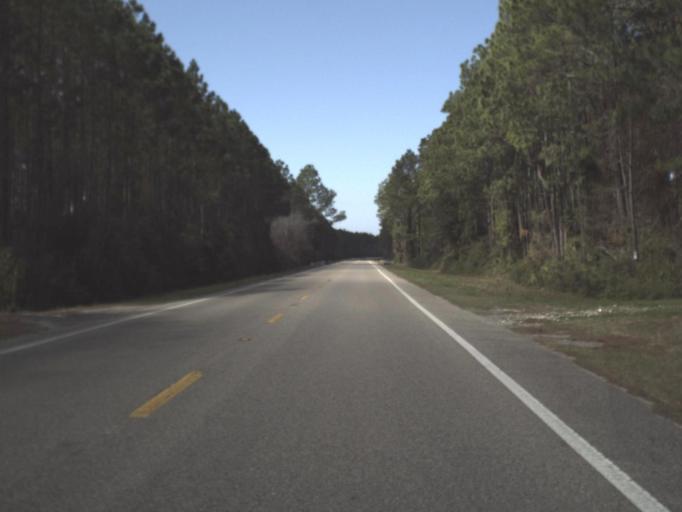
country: US
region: Florida
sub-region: Gulf County
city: Port Saint Joe
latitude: 29.7409
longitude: -85.2175
